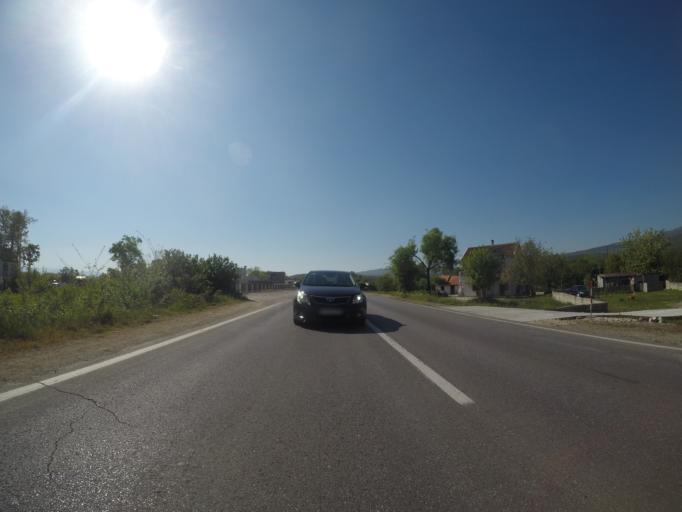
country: ME
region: Danilovgrad
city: Danilovgrad
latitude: 42.5297
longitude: 19.1166
